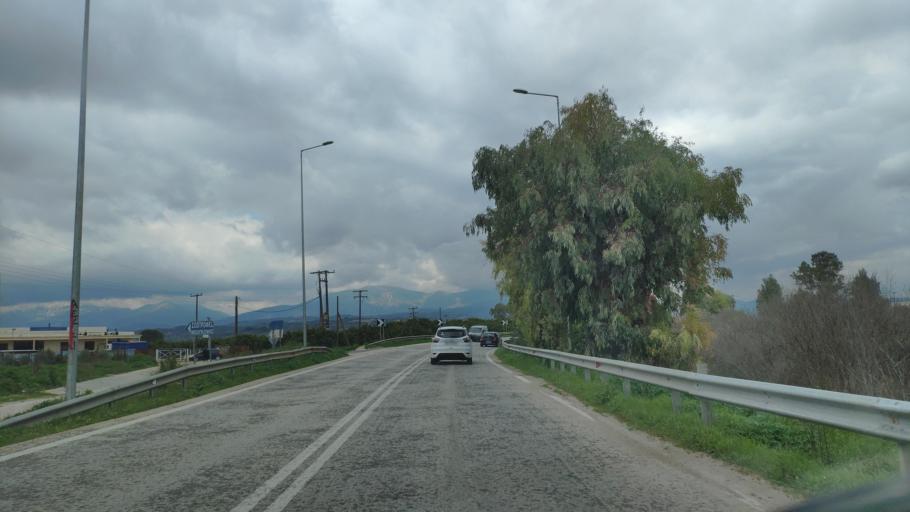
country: GR
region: Peloponnese
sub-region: Nomos Argolidos
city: Koutsopodi
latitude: 37.6707
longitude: 22.7203
